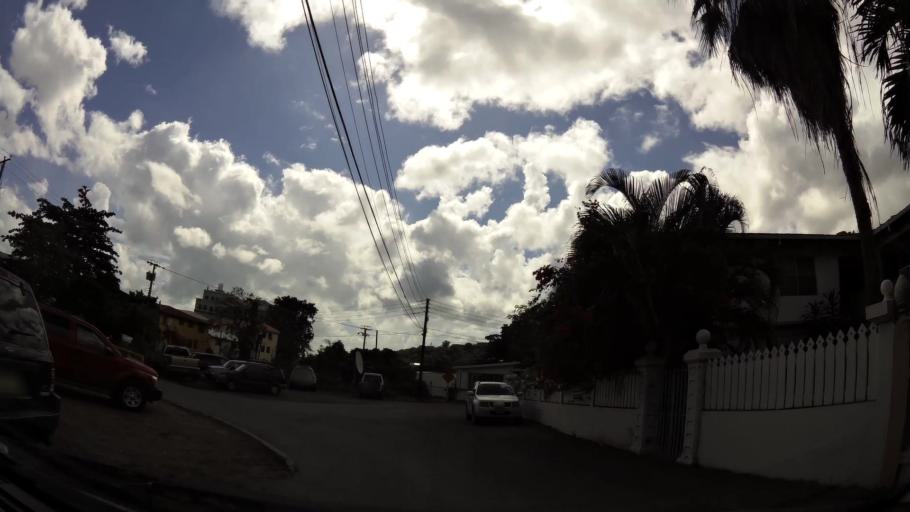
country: VG
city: Road Town
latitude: 18.4271
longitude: -64.6233
